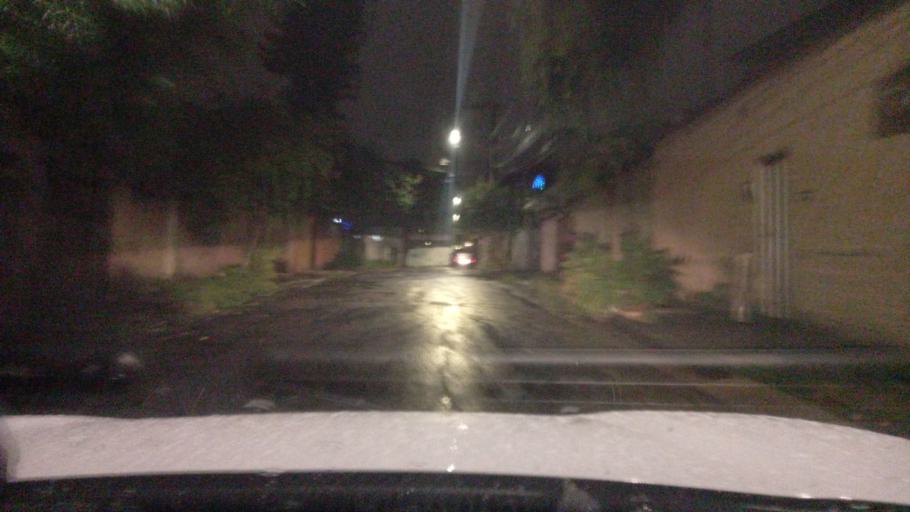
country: BR
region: Minas Gerais
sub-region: Belo Horizonte
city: Belo Horizonte
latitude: -19.9025
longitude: -43.9145
